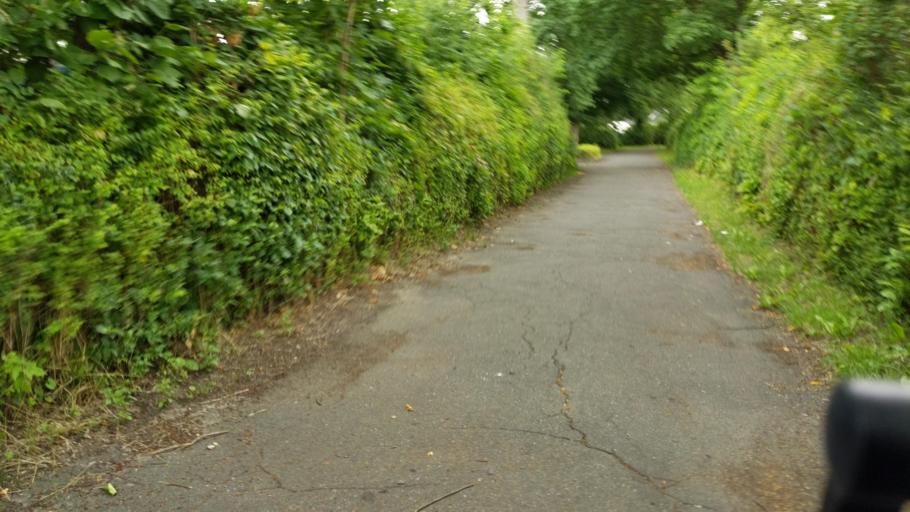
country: DE
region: Lower Saxony
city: Braunschweig
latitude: 52.2352
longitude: 10.5477
